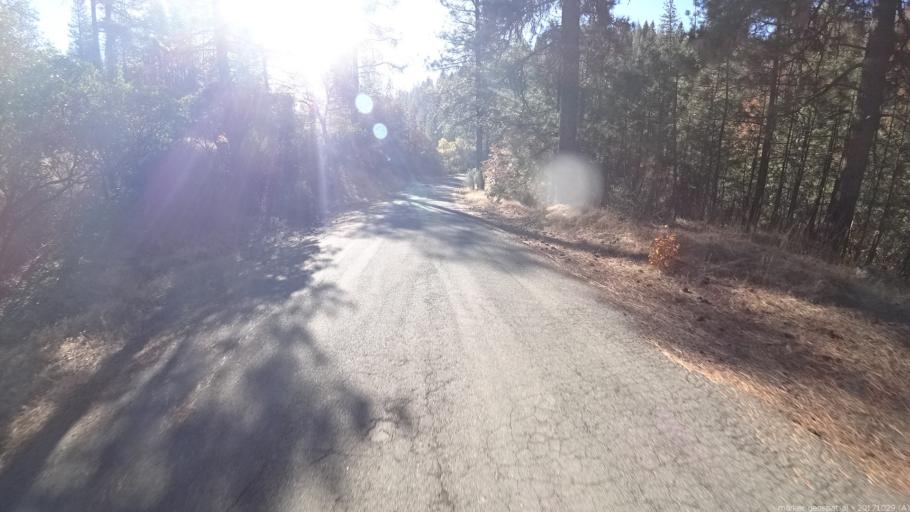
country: US
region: California
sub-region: Trinity County
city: Hayfork
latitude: 40.3675
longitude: -122.9718
